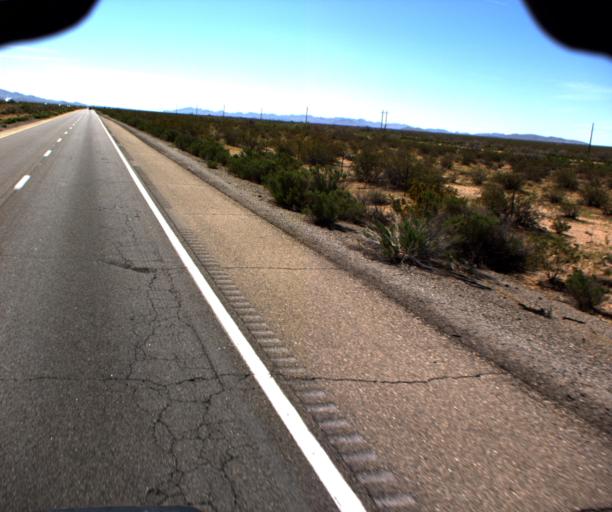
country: US
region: Arizona
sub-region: Mohave County
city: Dolan Springs
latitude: 35.6030
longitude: -114.4035
